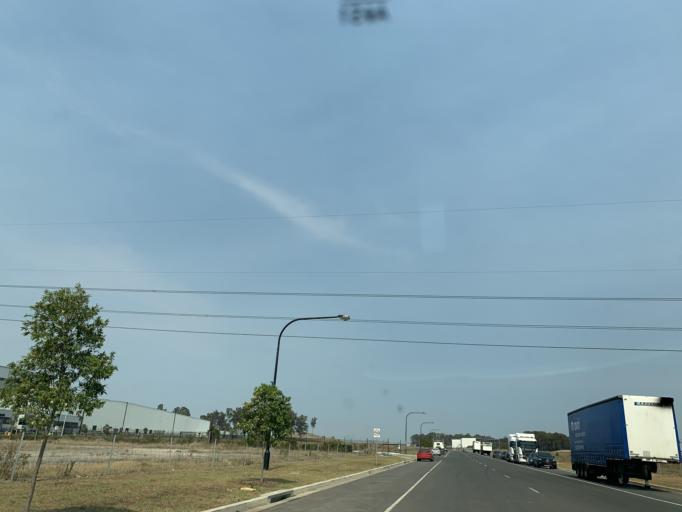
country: AU
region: New South Wales
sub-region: Blacktown
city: Blackett
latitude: -33.7179
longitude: 150.8208
